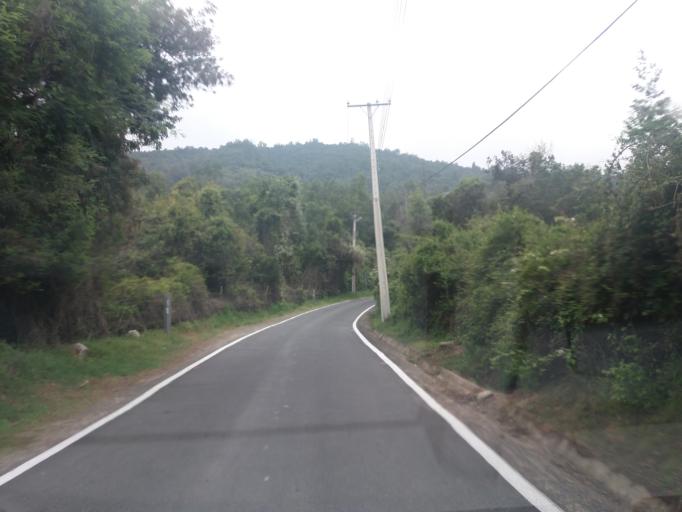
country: CL
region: Valparaiso
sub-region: Provincia de Marga Marga
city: Limache
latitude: -33.0210
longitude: -71.0713
